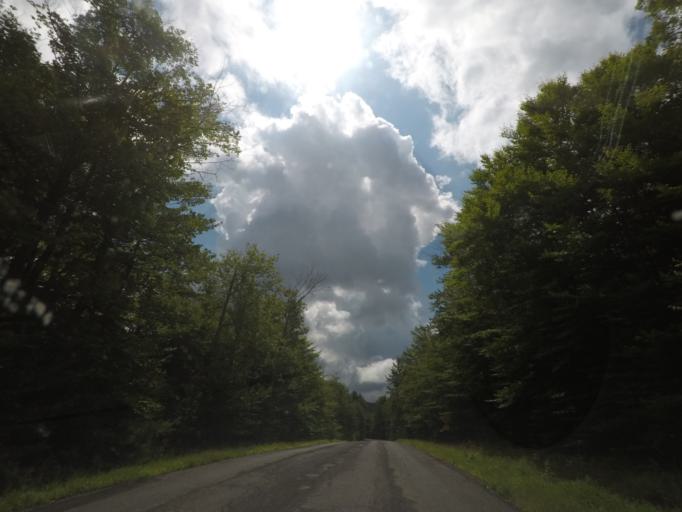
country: US
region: New York
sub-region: Rensselaer County
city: Averill Park
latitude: 42.6804
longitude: -73.4281
